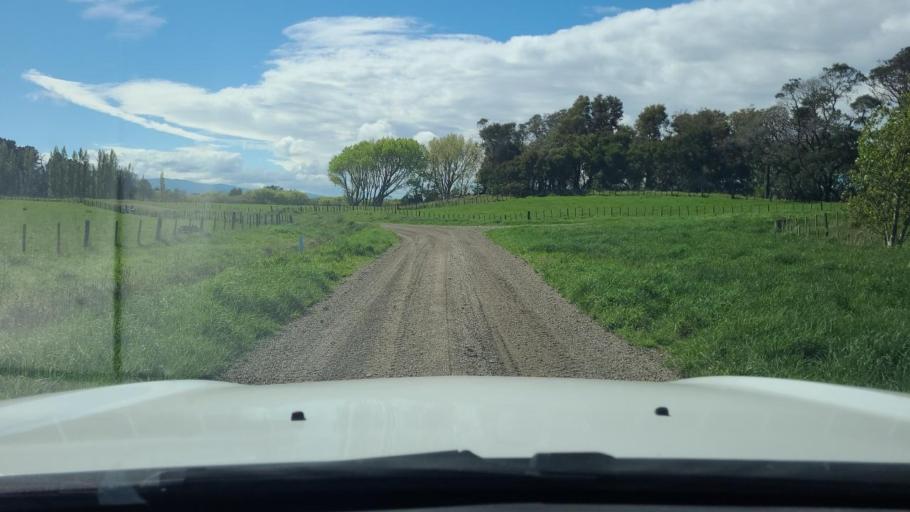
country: NZ
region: Wellington
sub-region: Upper Hutt City
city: Upper Hutt
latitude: -41.2626
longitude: 175.2781
